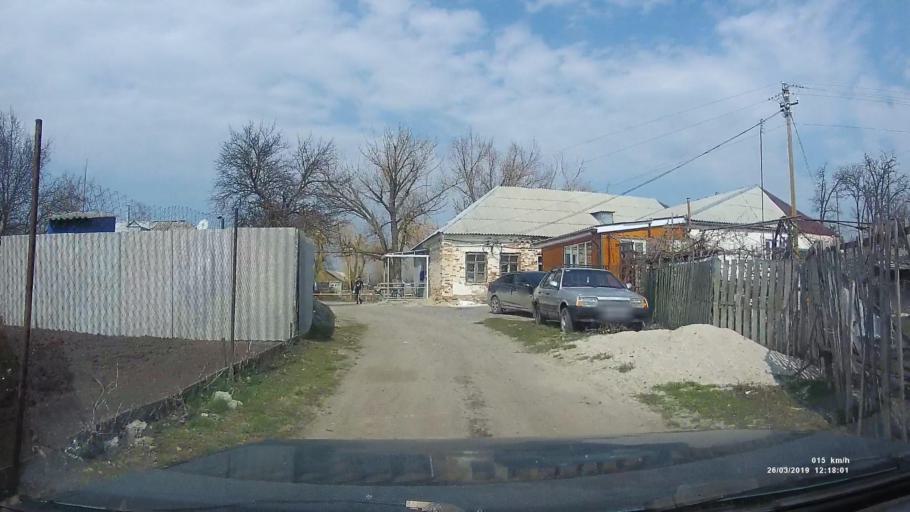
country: RU
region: Rostov
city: Novobessergenovka
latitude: 47.1463
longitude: 38.6426
